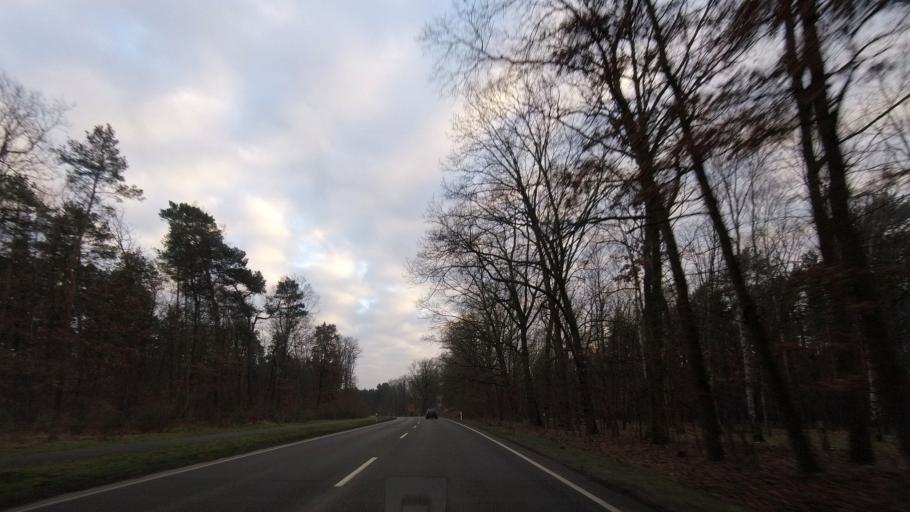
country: DE
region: Brandenburg
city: Michendorf
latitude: 52.3325
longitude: 13.0397
